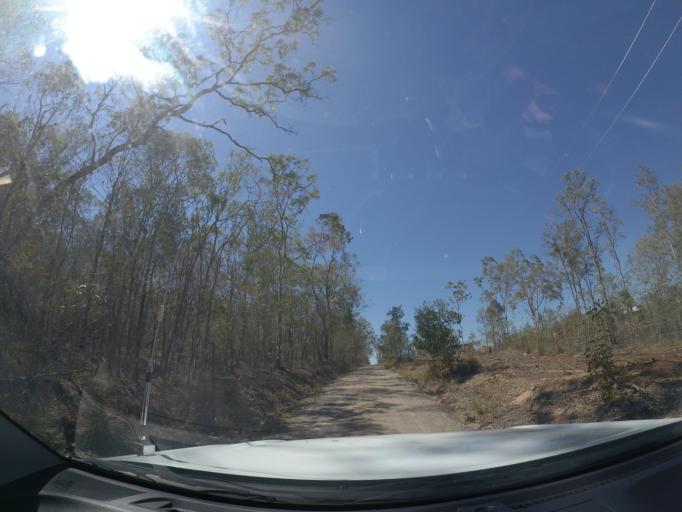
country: AU
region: Queensland
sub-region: Logan
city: North Maclean
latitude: -27.7569
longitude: 152.9418
